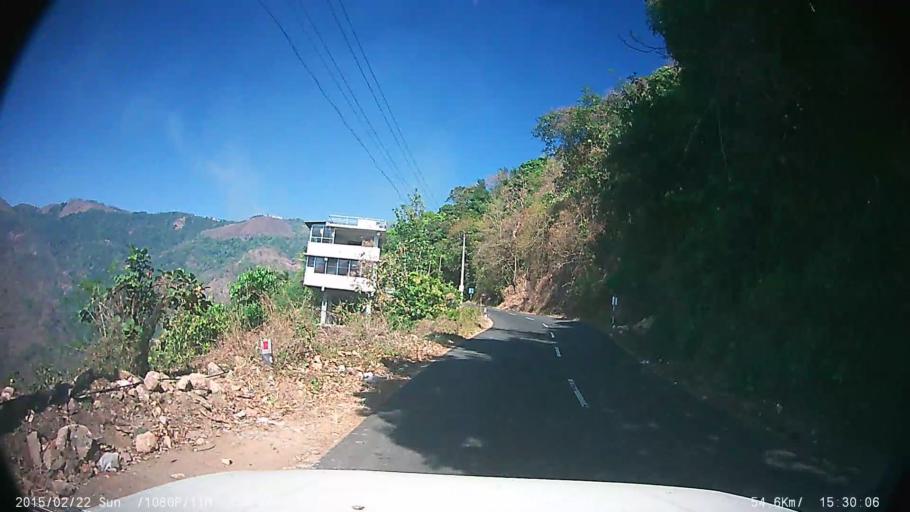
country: IN
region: Kerala
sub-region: Kottayam
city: Erattupetta
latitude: 9.5588
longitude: 76.9517
